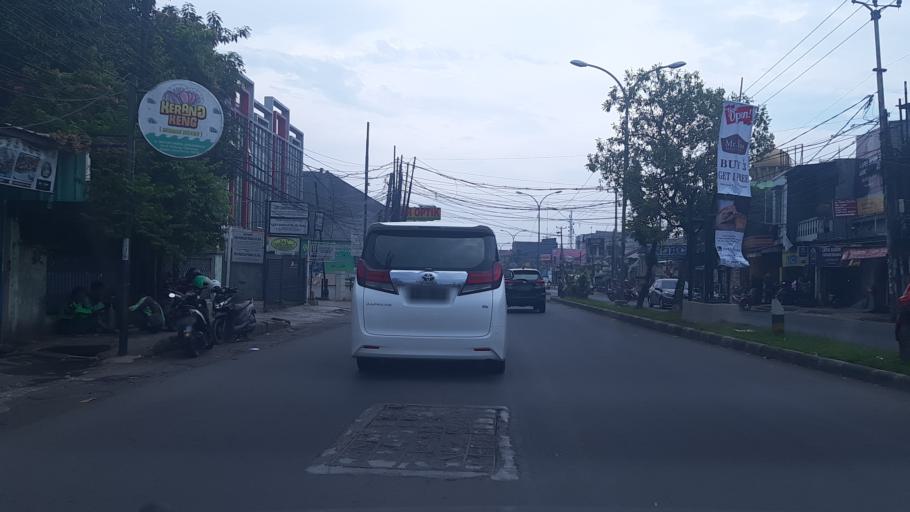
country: ID
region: West Java
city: Cibinong
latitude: -6.4732
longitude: 106.8629
